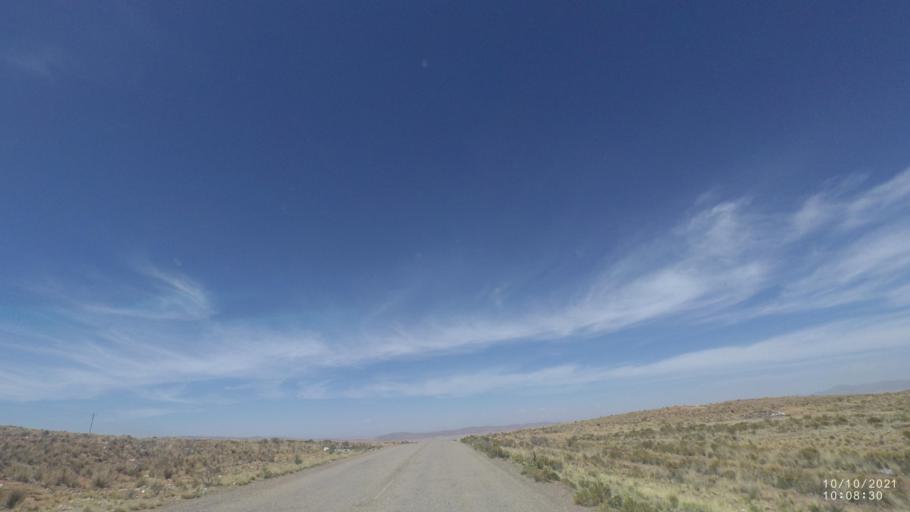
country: BO
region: La Paz
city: Eucaliptus
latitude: -17.3918
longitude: -67.4788
